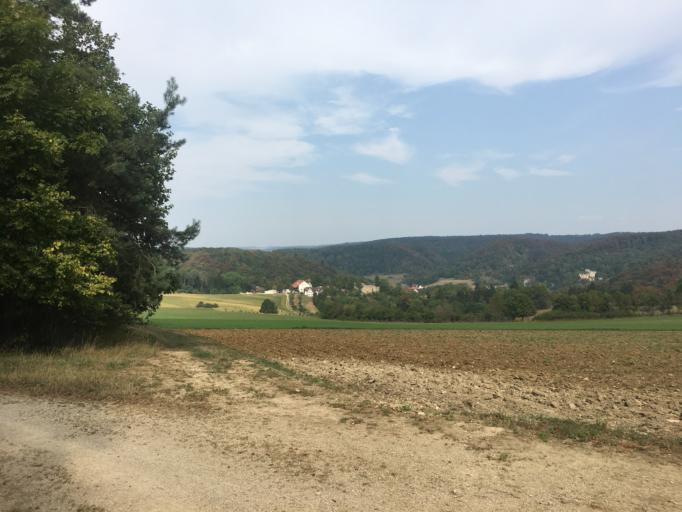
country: DE
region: Baden-Wuerttemberg
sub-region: Tuebingen Region
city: Hayingen
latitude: 48.2796
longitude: 9.4972
